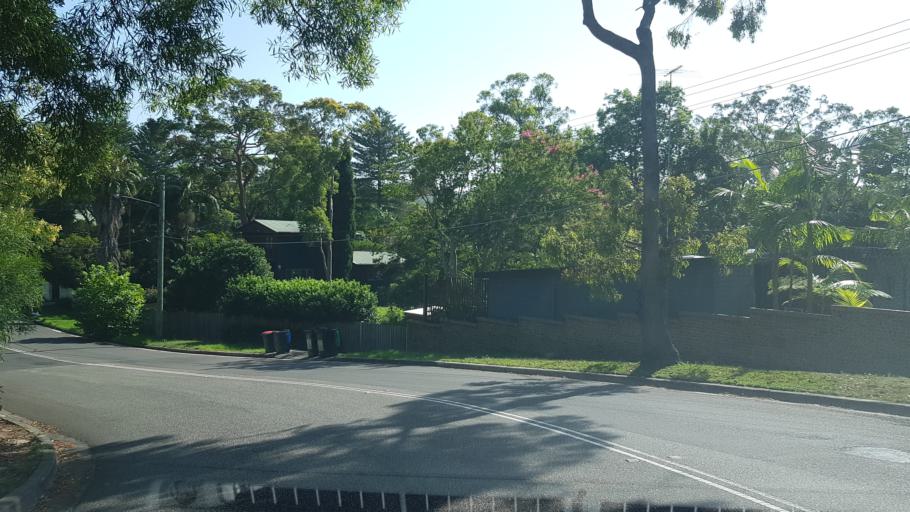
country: AU
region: New South Wales
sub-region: Warringah
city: Narraweena
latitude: -33.7361
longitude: 151.2722
